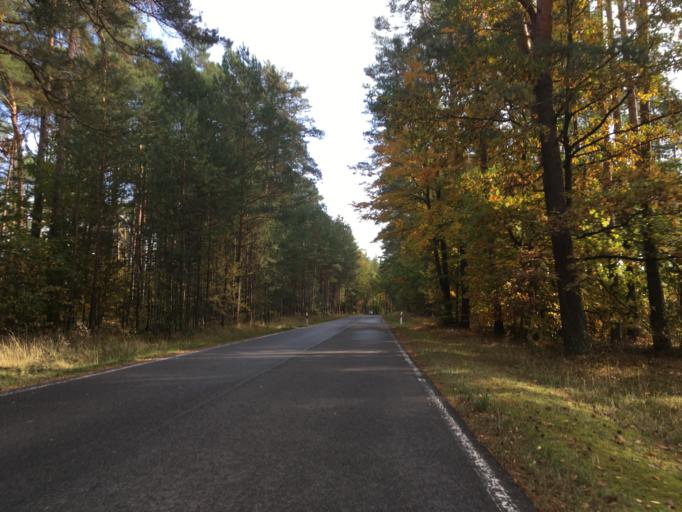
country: DE
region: Brandenburg
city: Templin
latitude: 53.0387
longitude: 13.4636
